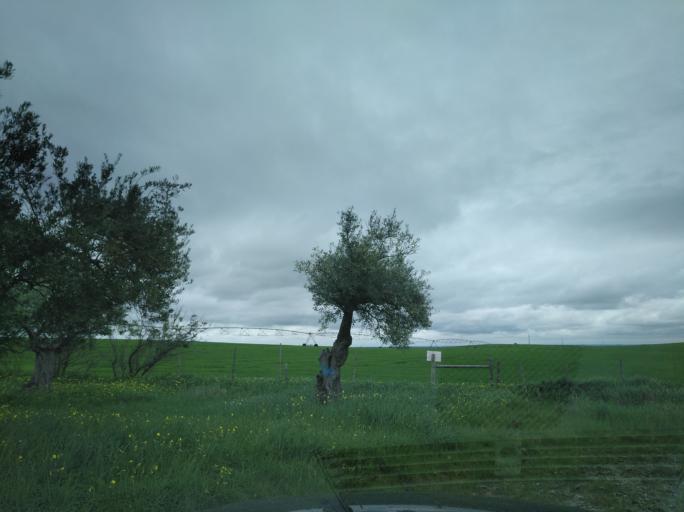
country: PT
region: Portalegre
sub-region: Campo Maior
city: Campo Maior
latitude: 38.9761
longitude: -7.0279
